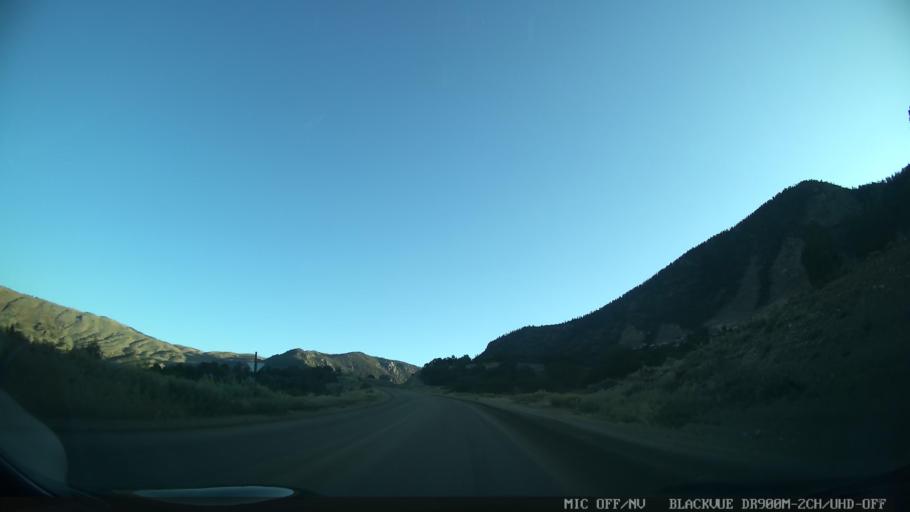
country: US
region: Colorado
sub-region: Grand County
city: Kremmling
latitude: 39.9853
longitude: -106.4941
